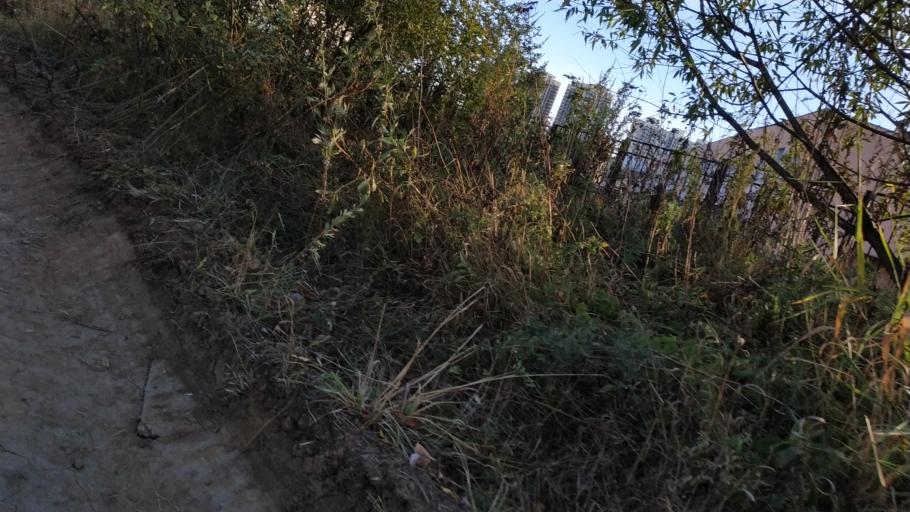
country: RU
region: Moscow
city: Novo-Peredelkino
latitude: 55.6439
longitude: 37.3337
